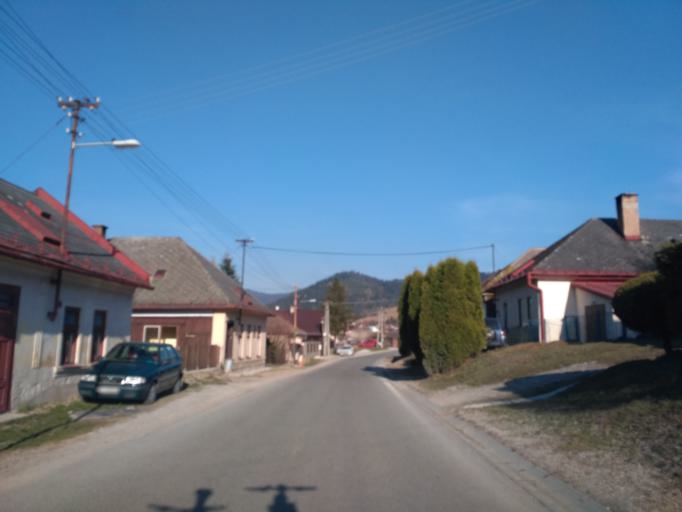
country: SK
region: Kosicky
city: Medzev
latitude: 48.7281
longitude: 20.7314
